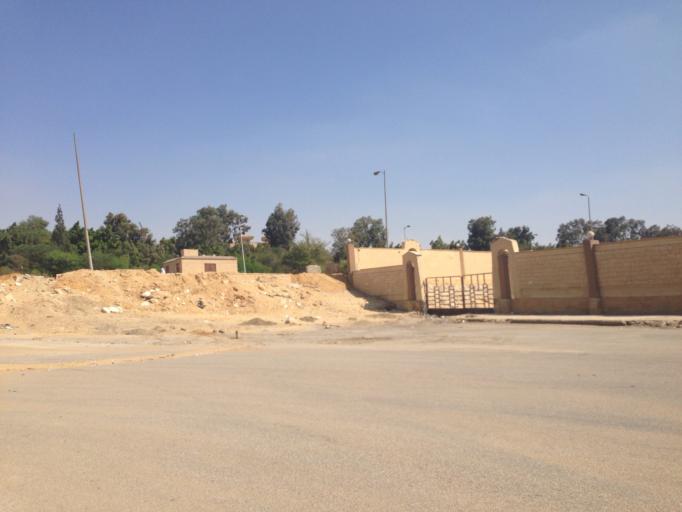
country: EG
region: Muhafazat al Qalyubiyah
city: Al Khankah
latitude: 30.0673
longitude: 31.4268
